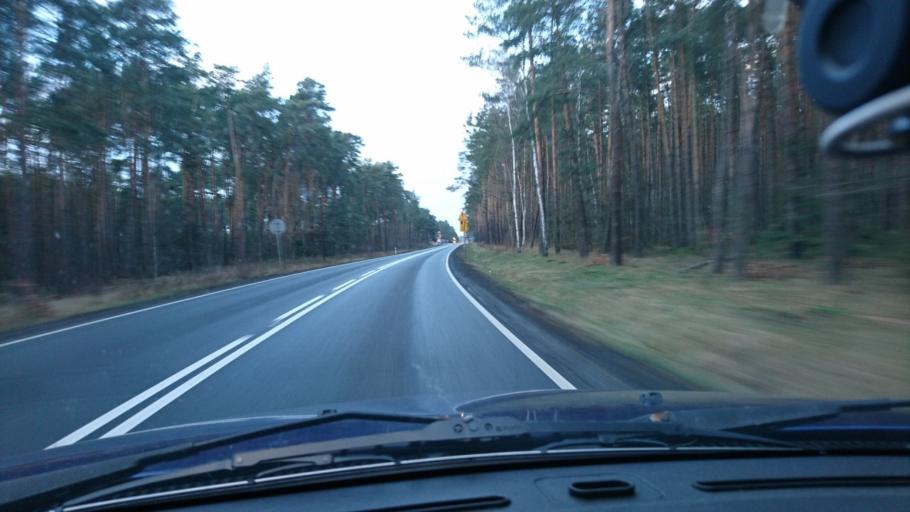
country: PL
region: Greater Poland Voivodeship
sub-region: Powiat kepinski
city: Kepno
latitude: 51.3378
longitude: 17.9536
